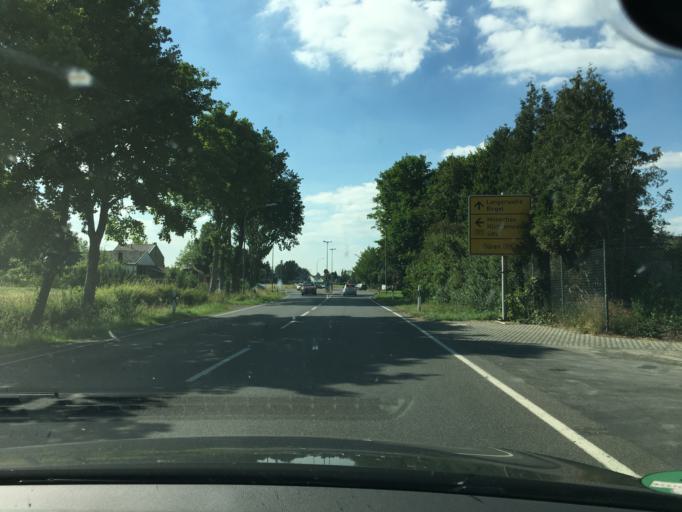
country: DE
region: North Rhine-Westphalia
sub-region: Regierungsbezirk Koln
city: Kreuzau
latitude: 50.7733
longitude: 6.4586
